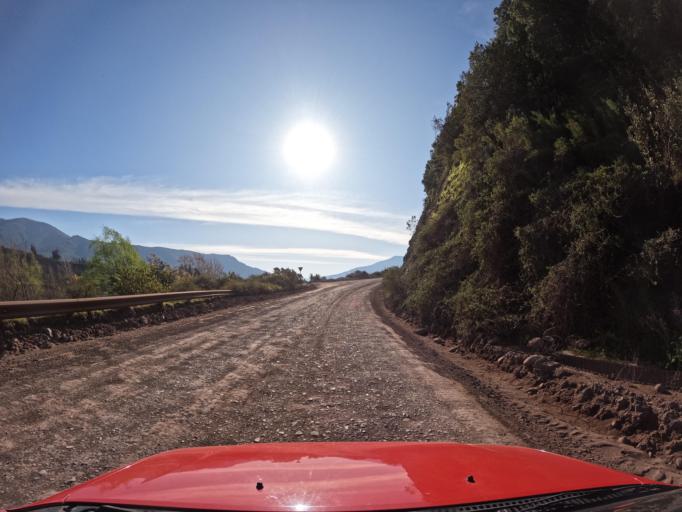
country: CL
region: Maule
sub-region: Provincia de Curico
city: Teno
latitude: -34.9981
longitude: -70.8447
